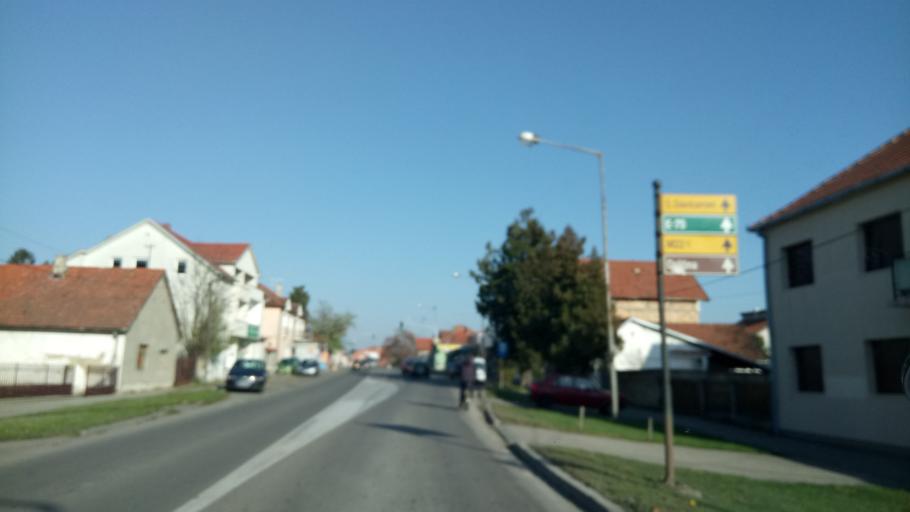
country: RS
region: Autonomna Pokrajina Vojvodina
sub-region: Sremski Okrug
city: Ingija
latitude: 45.0432
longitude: 20.0745
